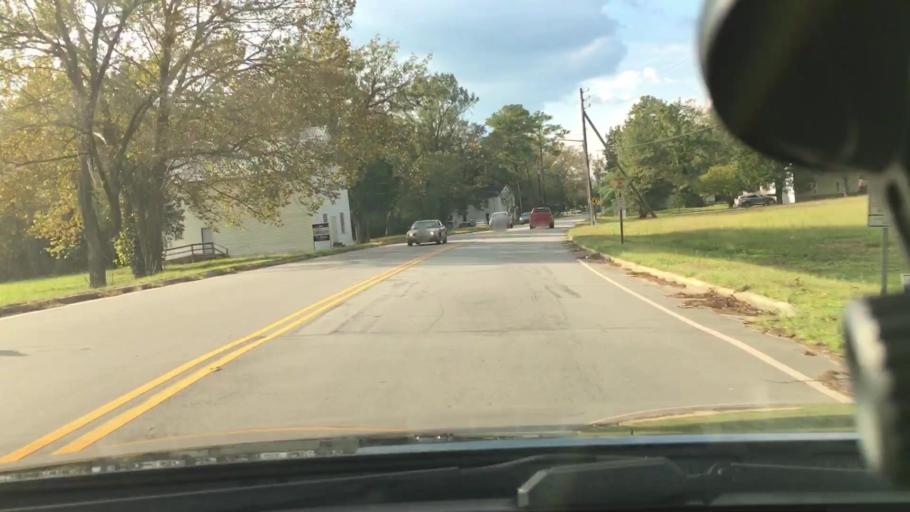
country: US
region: North Carolina
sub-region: Craven County
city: Vanceboro
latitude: 35.2955
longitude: -77.1468
